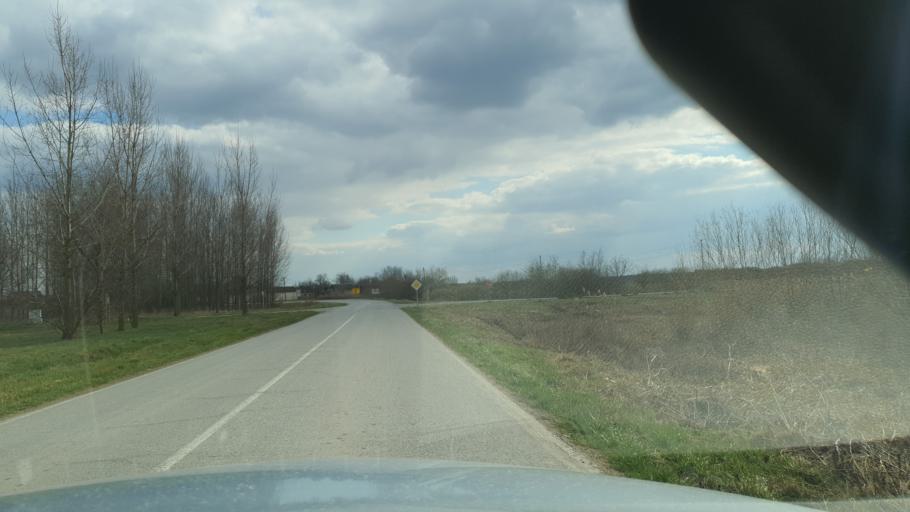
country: RS
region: Autonomna Pokrajina Vojvodina
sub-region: Juznobacki Okrug
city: Bac
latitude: 45.3902
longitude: 19.2198
